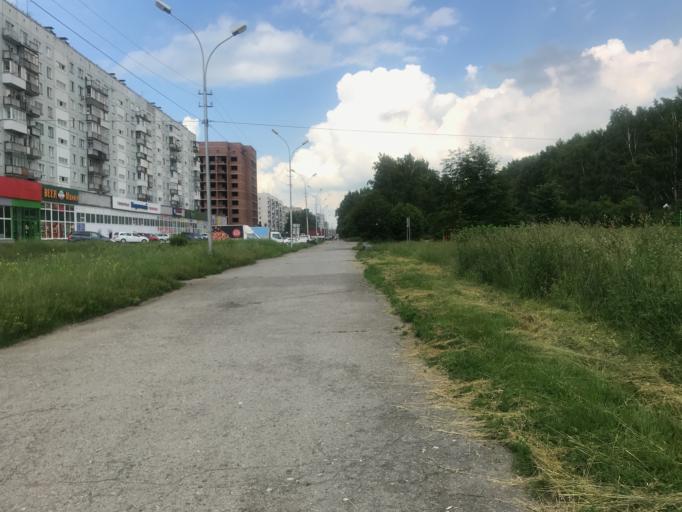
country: RU
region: Novosibirsk
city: Krasnoobsk
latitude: 54.9403
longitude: 82.9141
